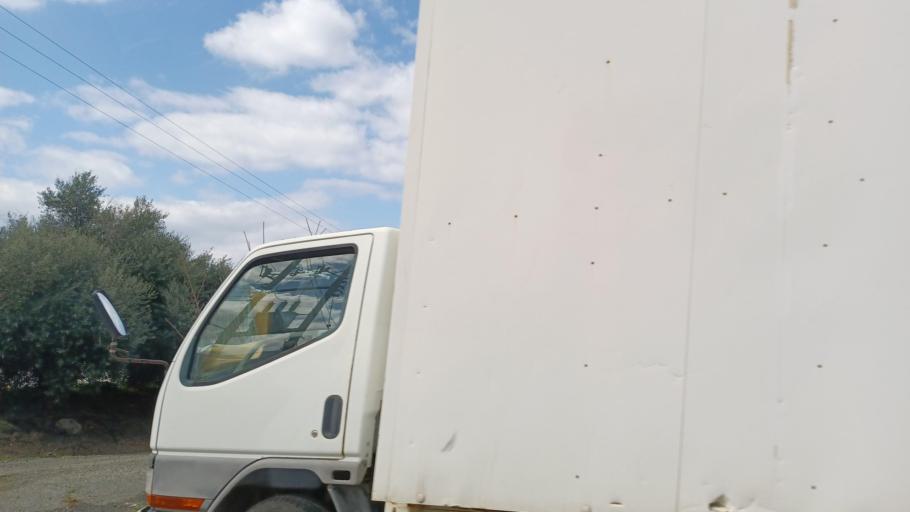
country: CY
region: Pafos
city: Polis
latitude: 35.1080
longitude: 32.5144
